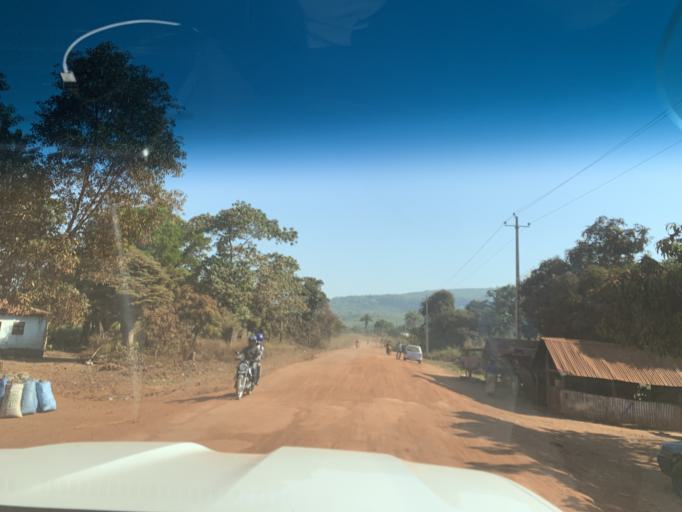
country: GN
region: Kindia
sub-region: Kindia
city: Kindia
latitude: 9.8676
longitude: -13.0562
